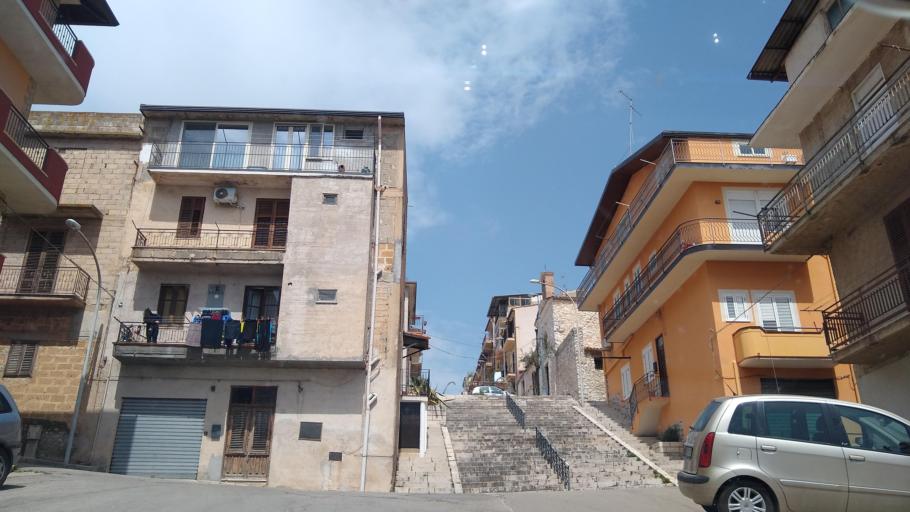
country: IT
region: Sicily
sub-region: Palermo
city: San Cipirello
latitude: 37.9608
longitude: 13.1741
